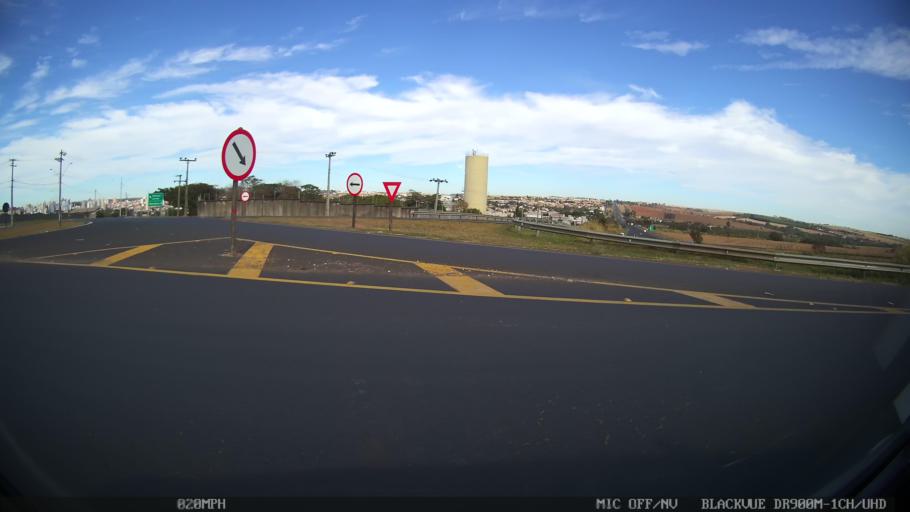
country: BR
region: Sao Paulo
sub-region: Catanduva
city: Catanduva
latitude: -21.1156
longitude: -48.9779
